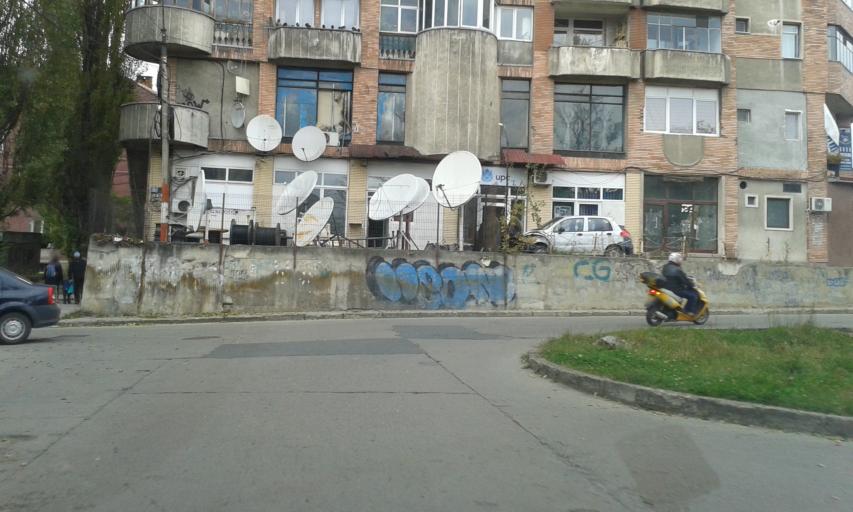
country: RO
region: Hunedoara
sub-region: Municipiul Petrosani
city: Petrosani
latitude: 45.4116
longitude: 23.3724
